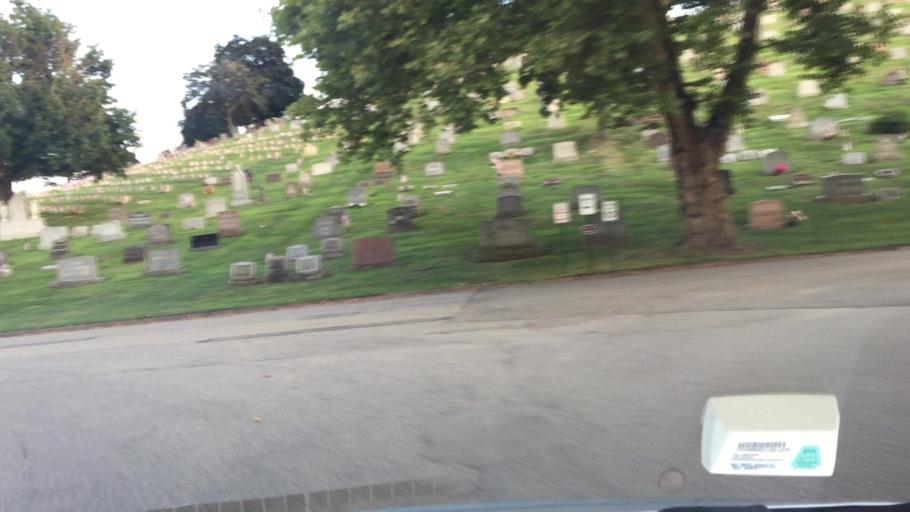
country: US
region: Pennsylvania
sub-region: Allegheny County
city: Homestead
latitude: 40.4187
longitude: -79.9289
